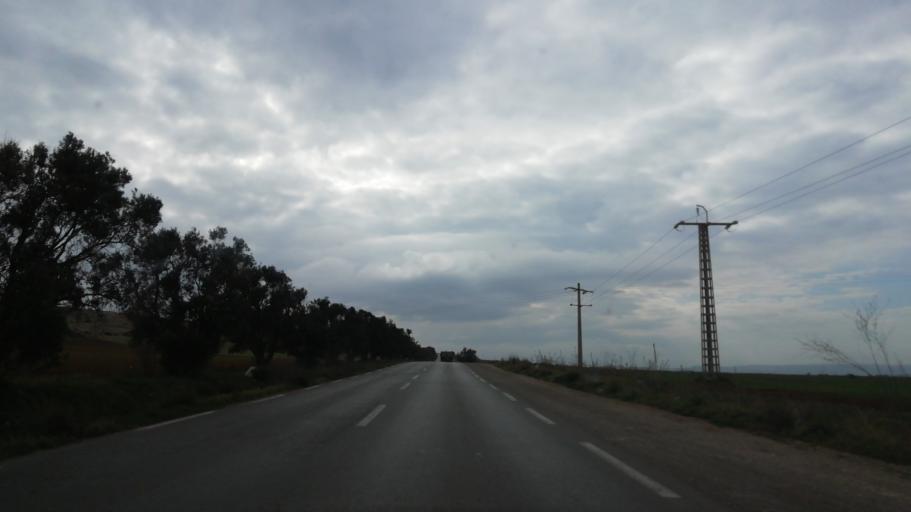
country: DZ
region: Oran
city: Ain el Bya
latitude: 35.7404
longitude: -0.3549
